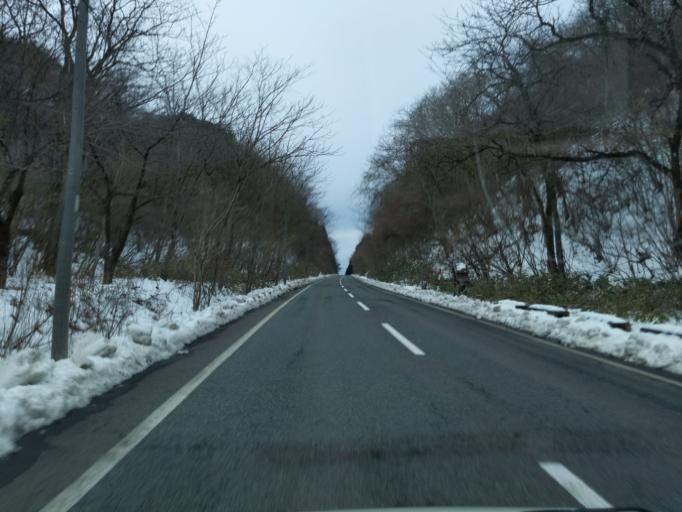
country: JP
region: Iwate
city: Mizusawa
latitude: 39.0933
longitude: 141.2703
